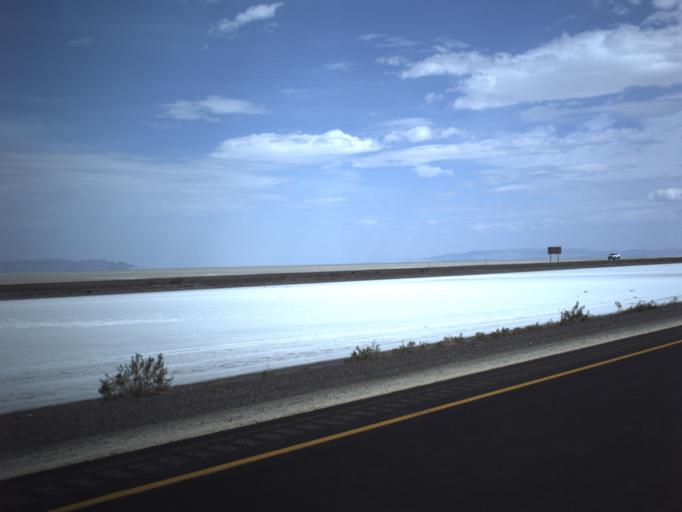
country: US
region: Utah
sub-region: Tooele County
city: Wendover
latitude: 40.7346
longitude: -113.6634
